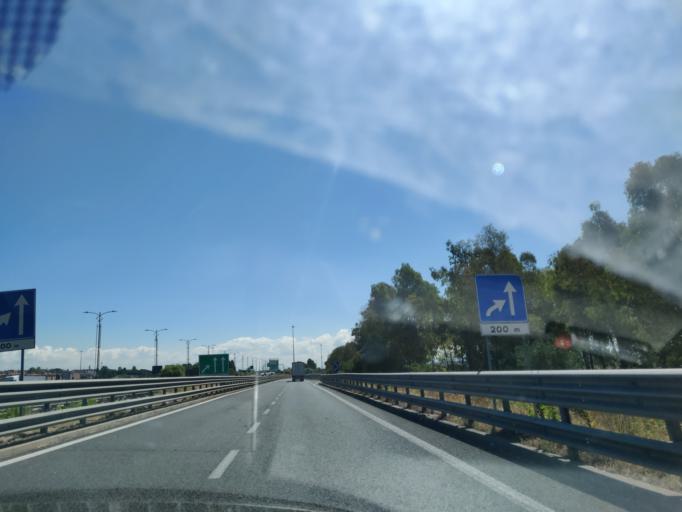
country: IT
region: Latium
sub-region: Citta metropolitana di Roma Capitale
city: Vitinia
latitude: 41.8173
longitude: 12.3825
